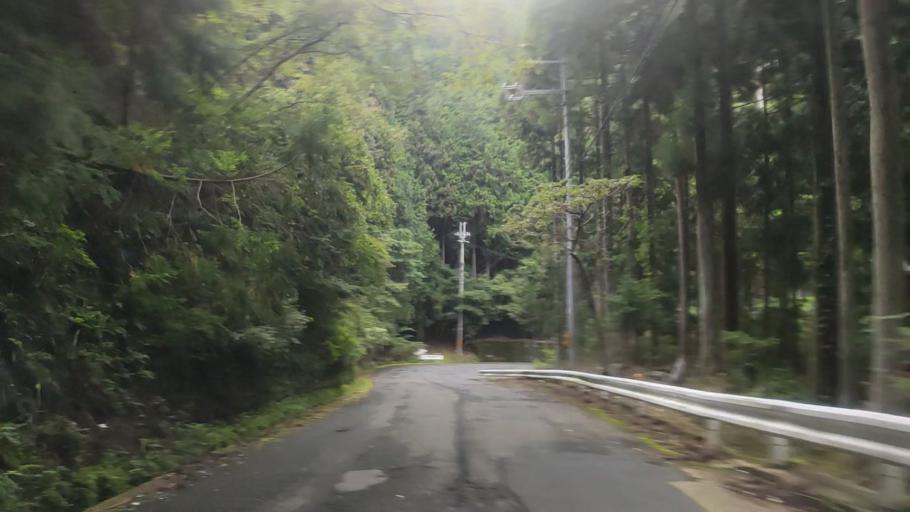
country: JP
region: Wakayama
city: Koya
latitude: 34.2258
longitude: 135.6204
